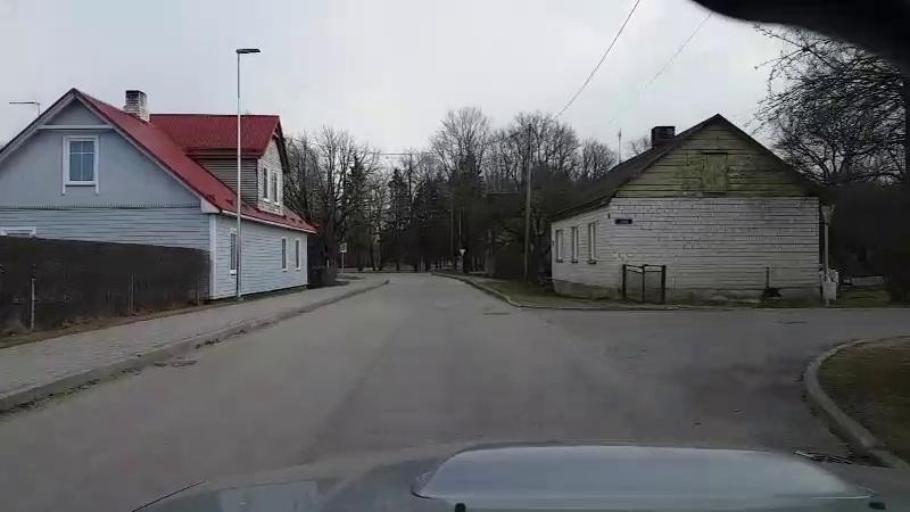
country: EE
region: Jaervamaa
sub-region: Paide linn
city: Paide
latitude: 58.8904
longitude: 25.5632
